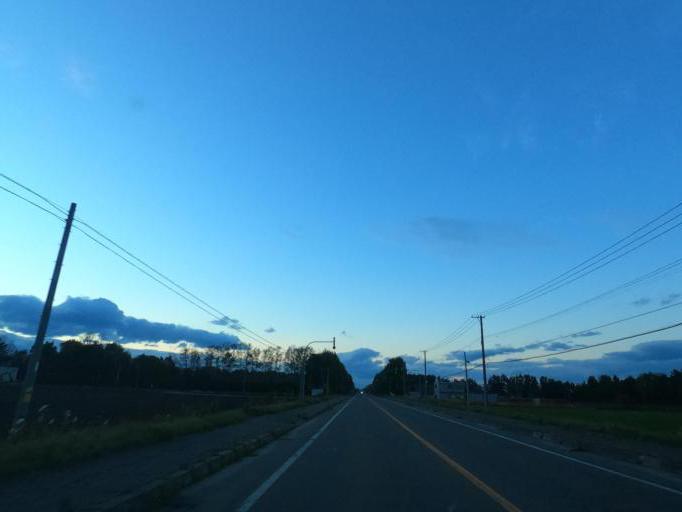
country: JP
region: Hokkaido
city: Obihiro
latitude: 42.6548
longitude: 143.1882
